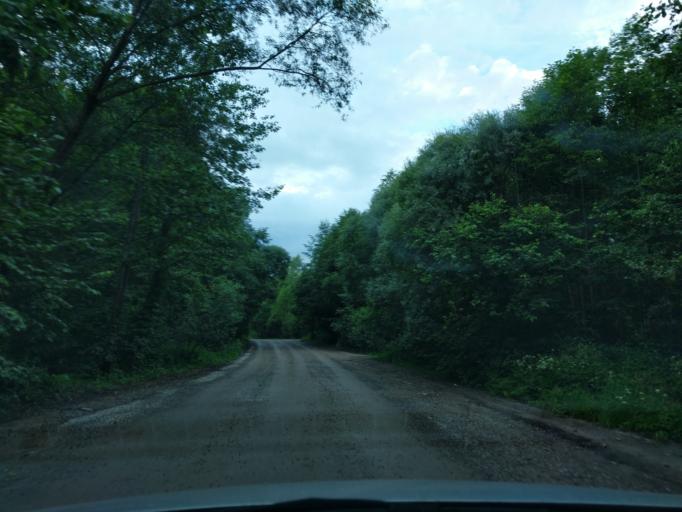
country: RU
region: Kaluga
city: Myatlevo
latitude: 54.8425
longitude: 35.6200
